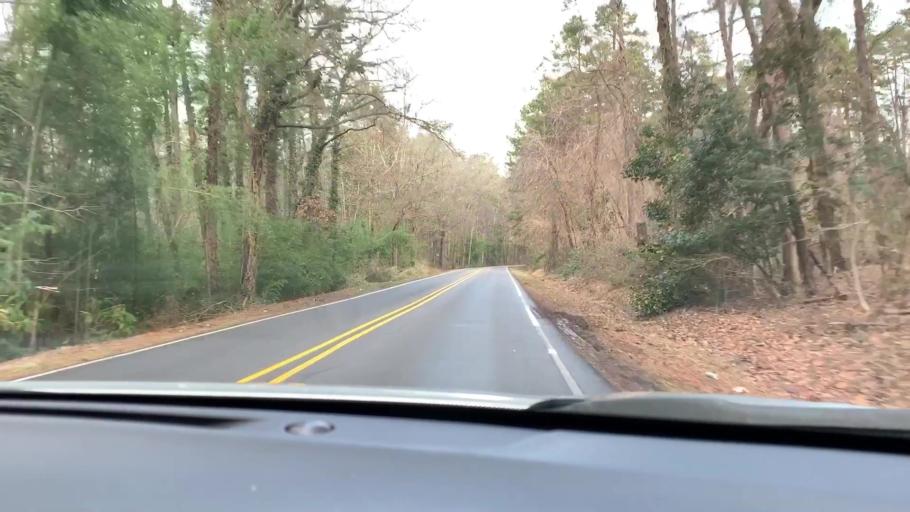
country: US
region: North Carolina
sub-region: Durham County
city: Durham
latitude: 35.9785
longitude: -78.9424
